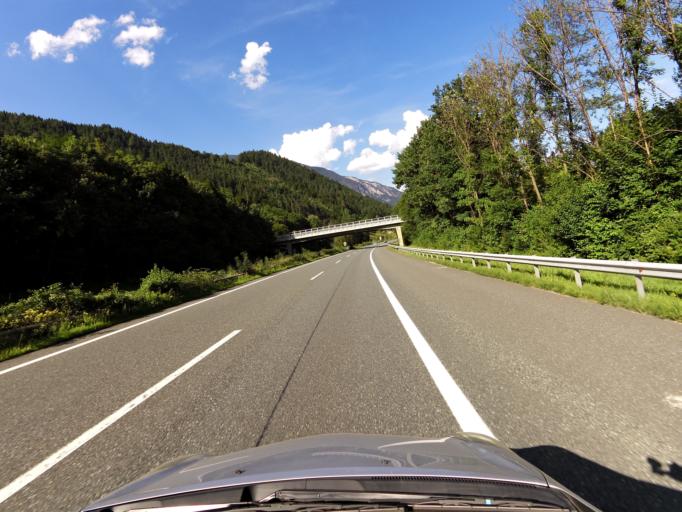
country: AT
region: Tyrol
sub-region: Politischer Bezirk Schwaz
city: Schwaz
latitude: 47.3571
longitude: 11.7004
